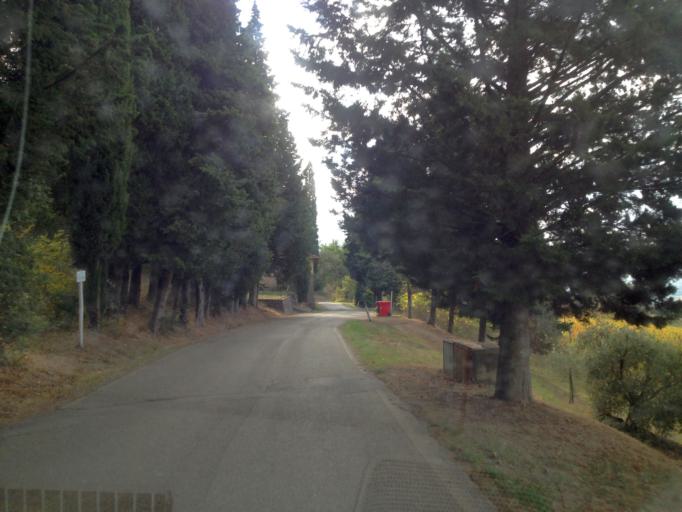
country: IT
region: Tuscany
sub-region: Province of Florence
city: Dicomano
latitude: 43.8596
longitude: 11.5075
